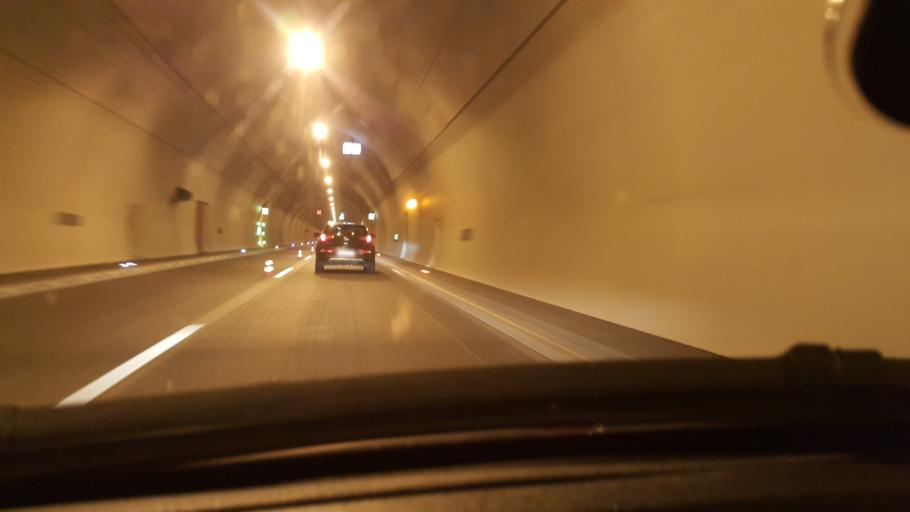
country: SI
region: Koper-Capodistria
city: Koper
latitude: 45.5404
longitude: 13.7097
